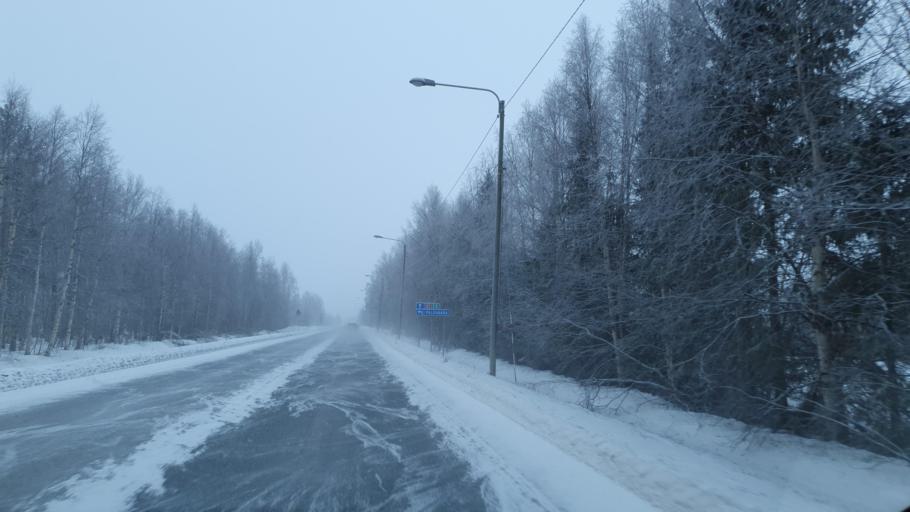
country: FI
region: Lapland
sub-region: Kemi-Tornio
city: Tornio
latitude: 66.0620
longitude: 23.9952
